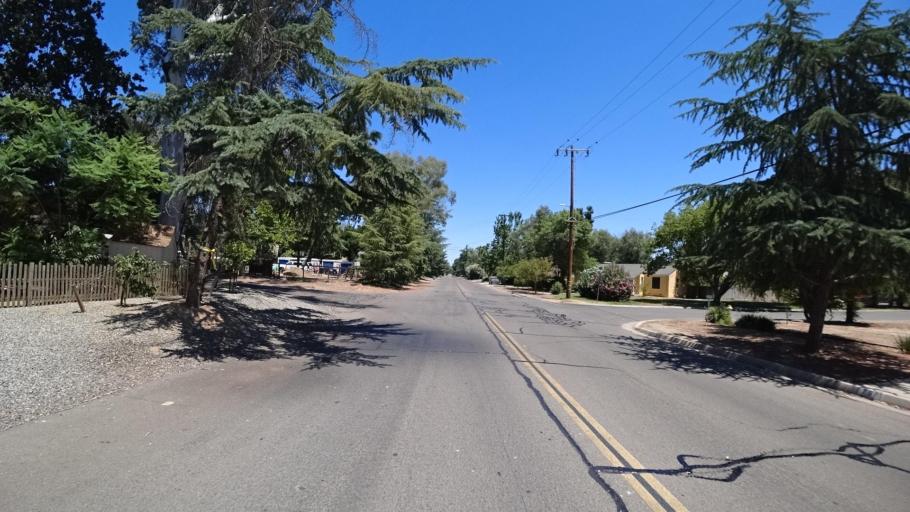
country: US
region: California
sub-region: Fresno County
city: Fresno
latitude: 36.7892
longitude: -119.8024
